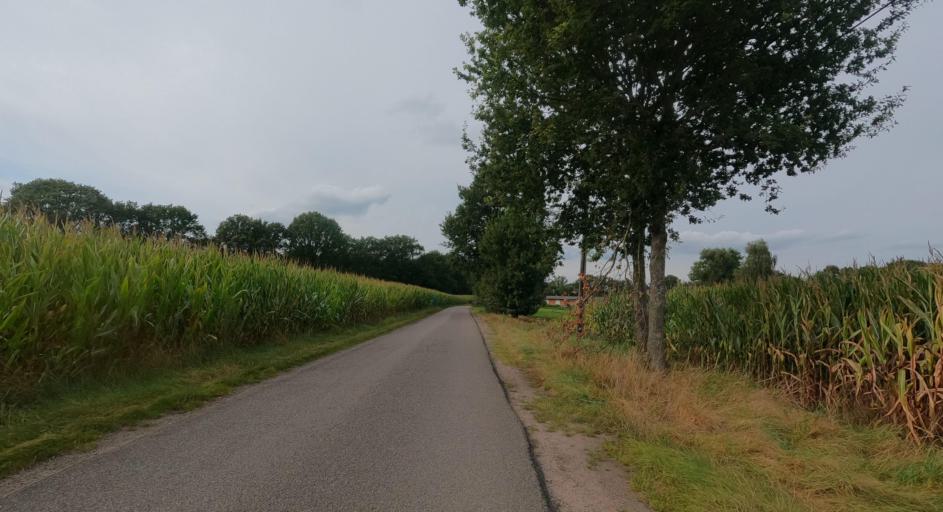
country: BE
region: Flanders
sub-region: Provincie Antwerpen
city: Essen
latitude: 51.4589
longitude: 4.5089
